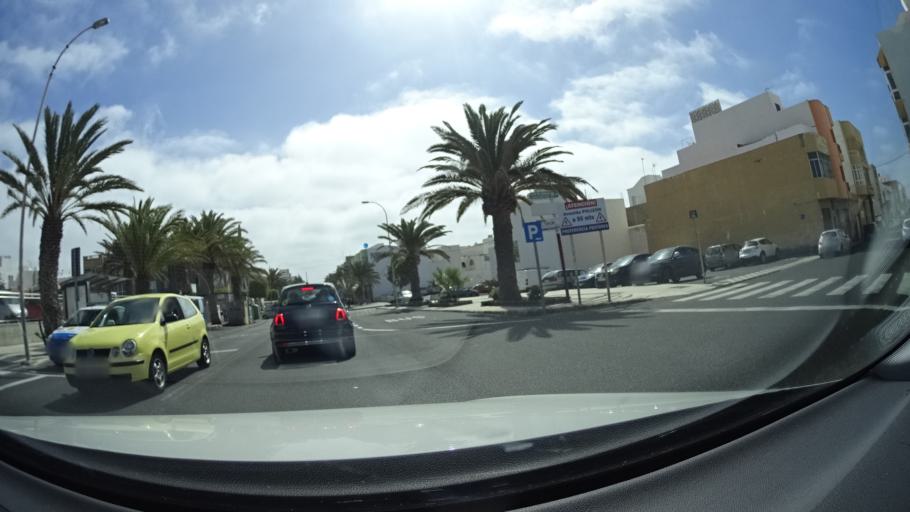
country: ES
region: Canary Islands
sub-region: Provincia de Las Palmas
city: Cruce de Arinaga
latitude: 27.8584
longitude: -15.3974
